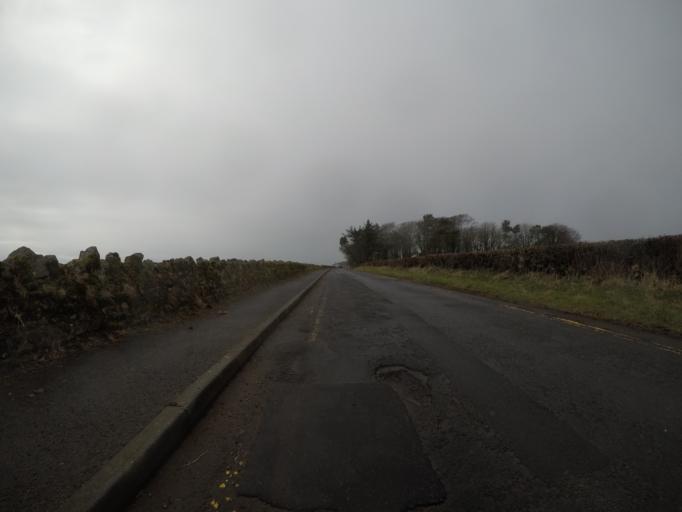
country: GB
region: Scotland
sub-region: North Ayrshire
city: West Kilbride
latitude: 55.6957
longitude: -4.8730
